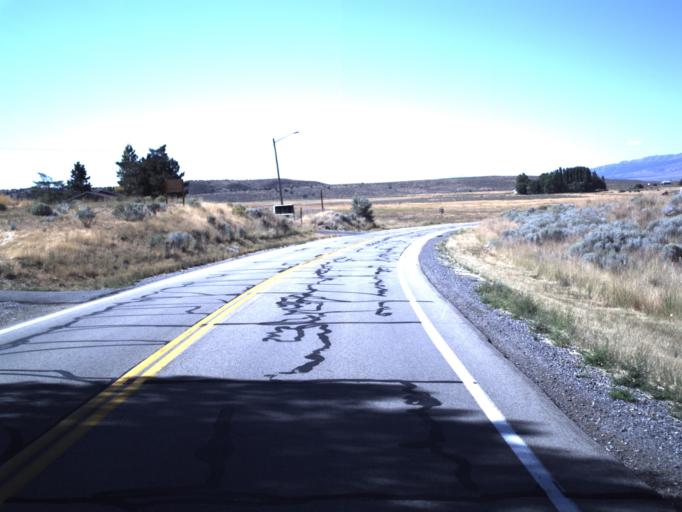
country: US
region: Utah
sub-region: Tooele County
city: Tooele
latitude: 40.4484
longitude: -112.3635
